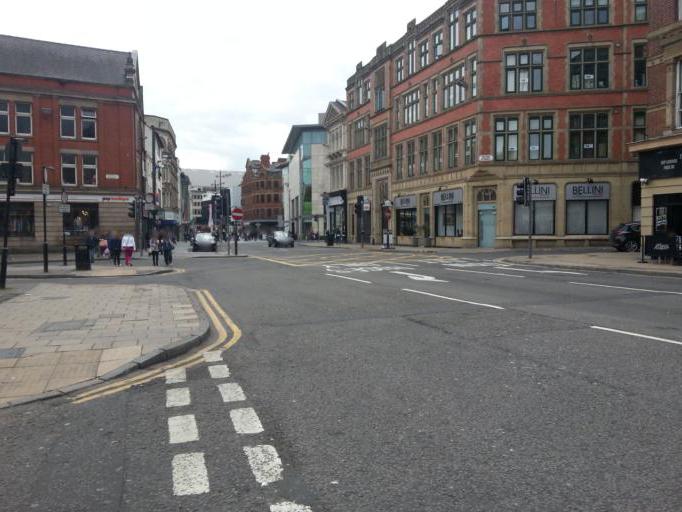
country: GB
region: England
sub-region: Liverpool
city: Liverpool
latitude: 53.4073
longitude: -2.9843
